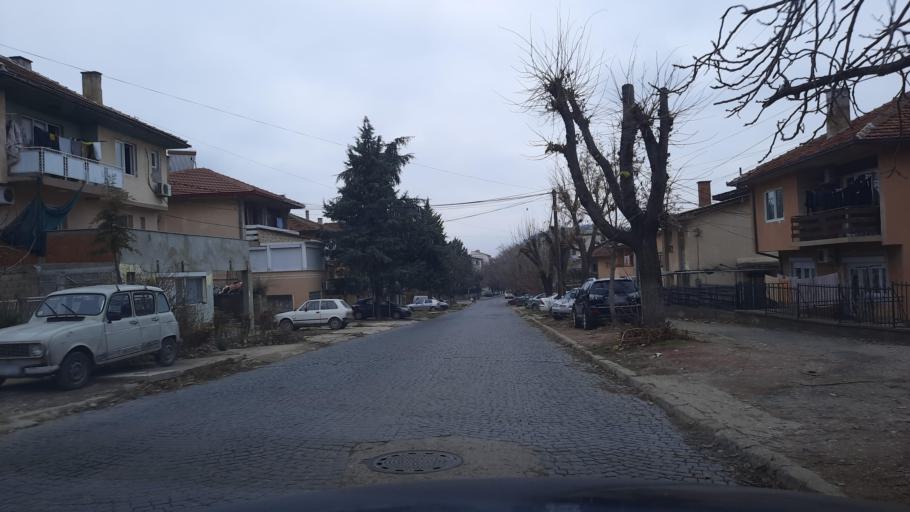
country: MK
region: Stip
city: Shtip
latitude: 41.7451
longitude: 22.2013
